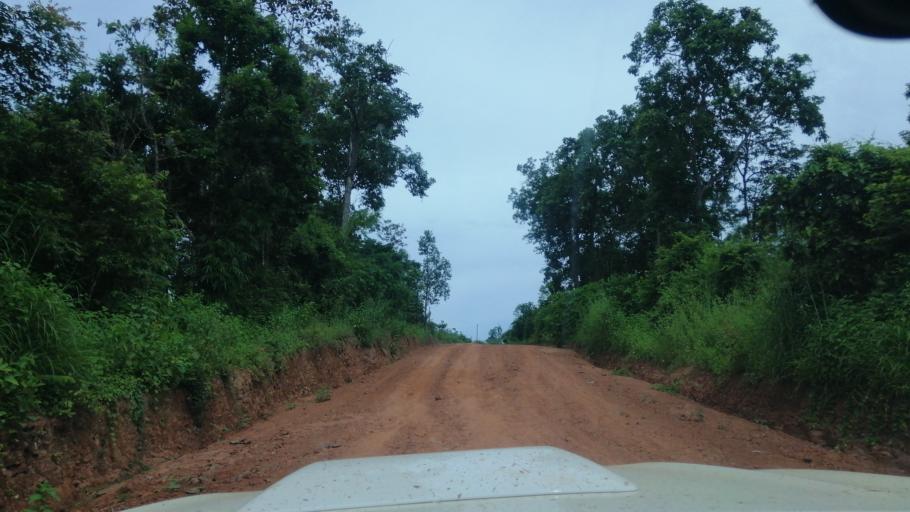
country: TH
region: Loei
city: Na Haeo
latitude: 17.5932
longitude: 101.1307
